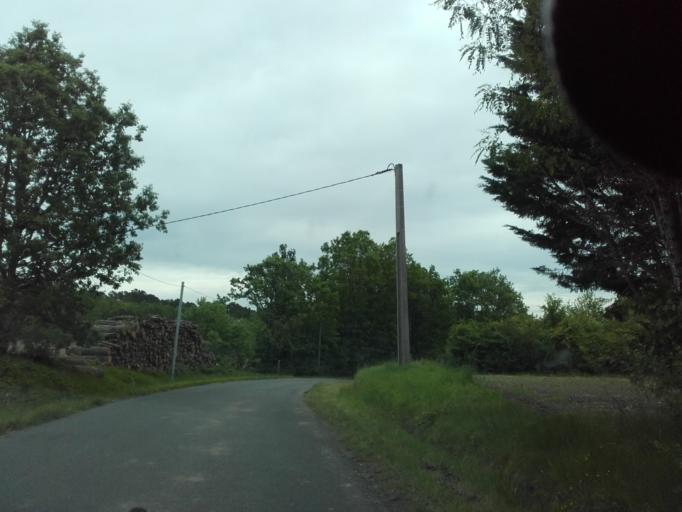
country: FR
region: Aquitaine
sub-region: Departement de la Dordogne
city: Monbazillac
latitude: 44.7763
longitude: 0.4701
